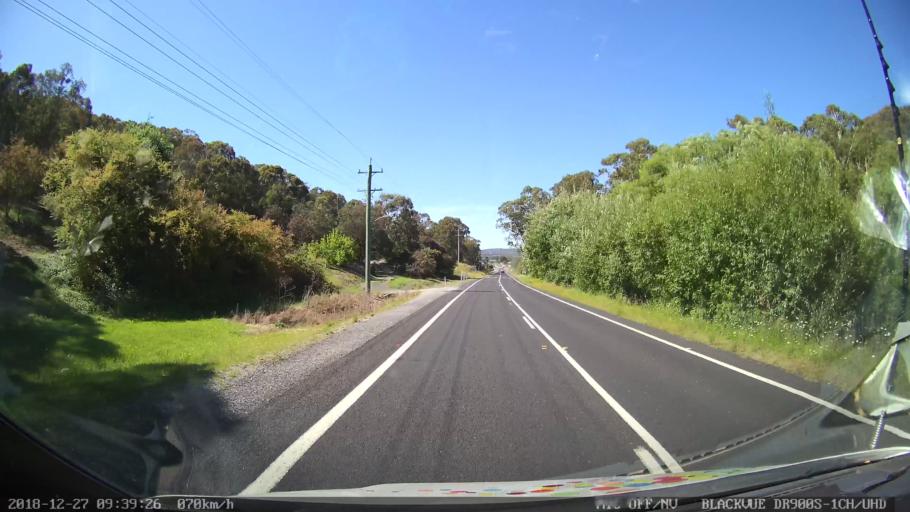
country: AU
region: New South Wales
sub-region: Lithgow
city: Portland
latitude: -33.2928
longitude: 150.0351
